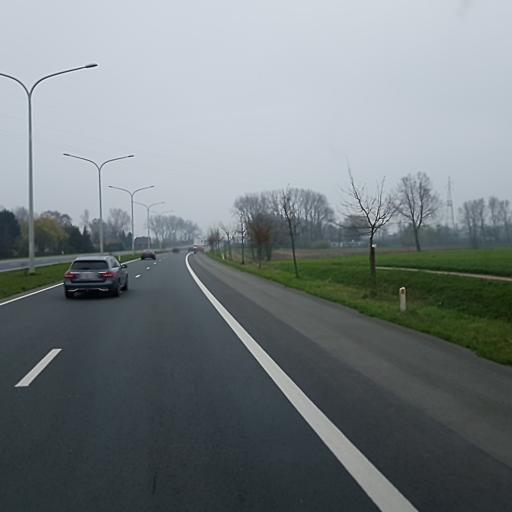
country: BE
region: Flanders
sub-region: Provincie Oost-Vlaanderen
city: Sint-Niklaas
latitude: 51.1403
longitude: 4.1392
